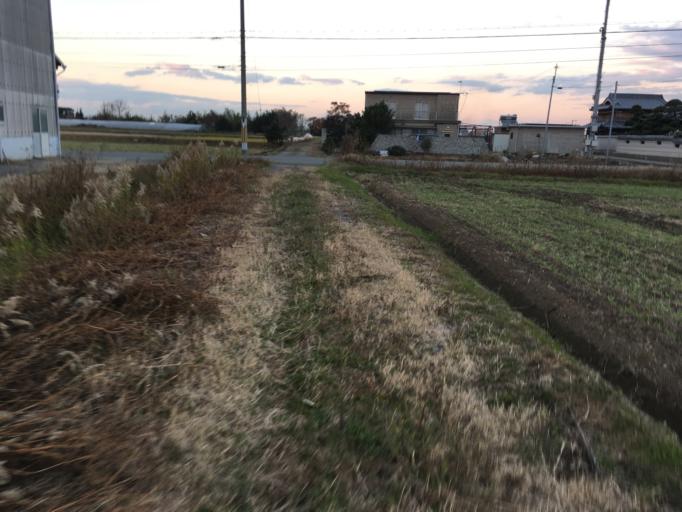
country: JP
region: Hyogo
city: Miki
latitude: 34.7375
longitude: 134.9503
